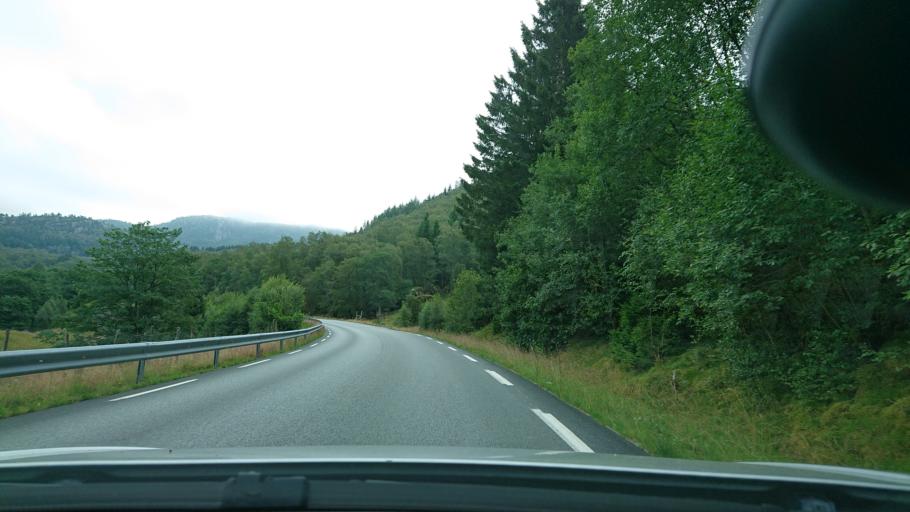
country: NO
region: Rogaland
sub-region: Hjelmeland
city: Hjelmelandsvagen
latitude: 59.2179
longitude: 6.2192
